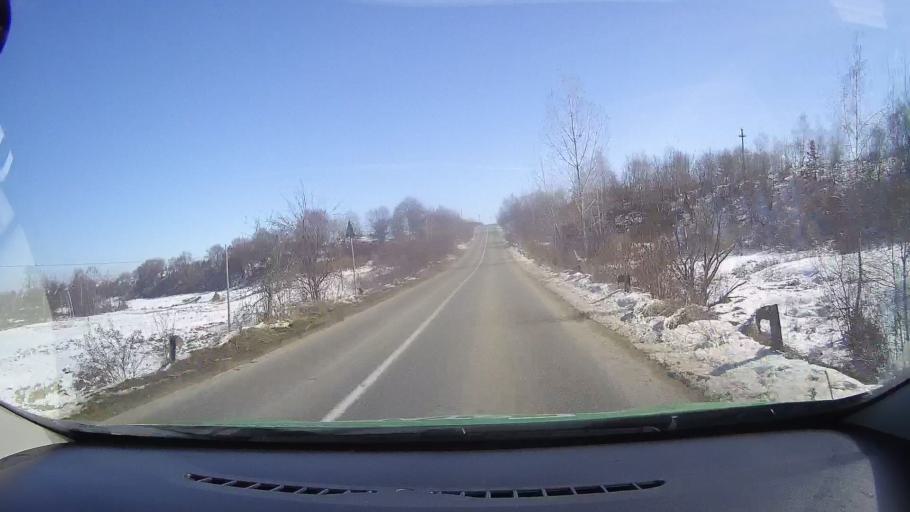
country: RO
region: Brasov
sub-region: Oras Victoria
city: Victoria
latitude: 45.7305
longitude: 24.7132
